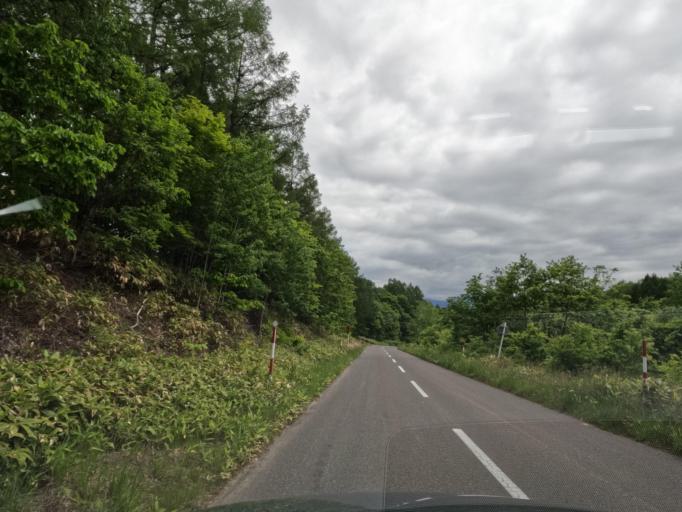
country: JP
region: Hokkaido
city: Shimo-furano
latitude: 43.4952
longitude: 142.4177
